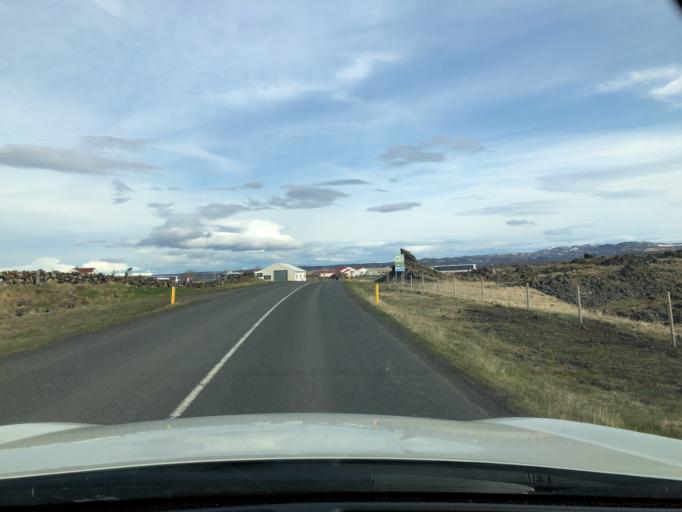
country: IS
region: Northeast
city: Laugar
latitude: 65.6181
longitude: -16.9173
